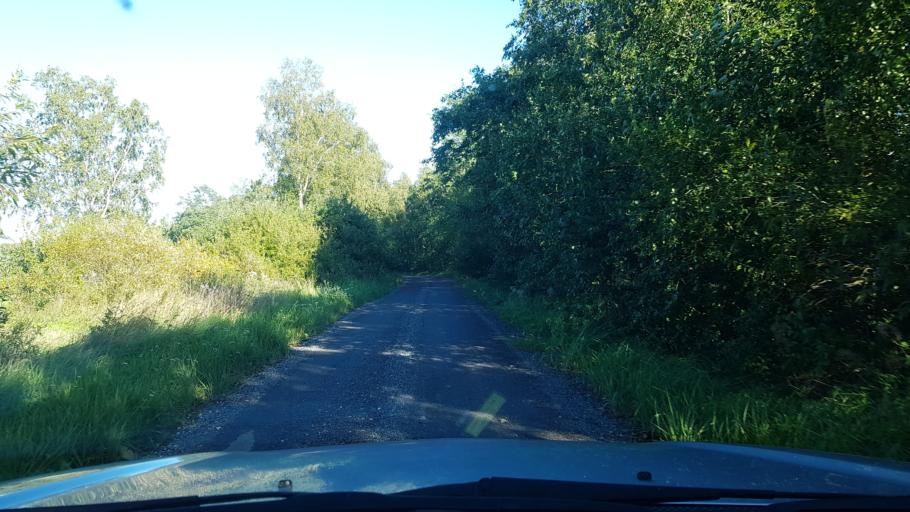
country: EE
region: Harju
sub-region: Tallinna linn
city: Kose
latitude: 59.4093
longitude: 24.8832
